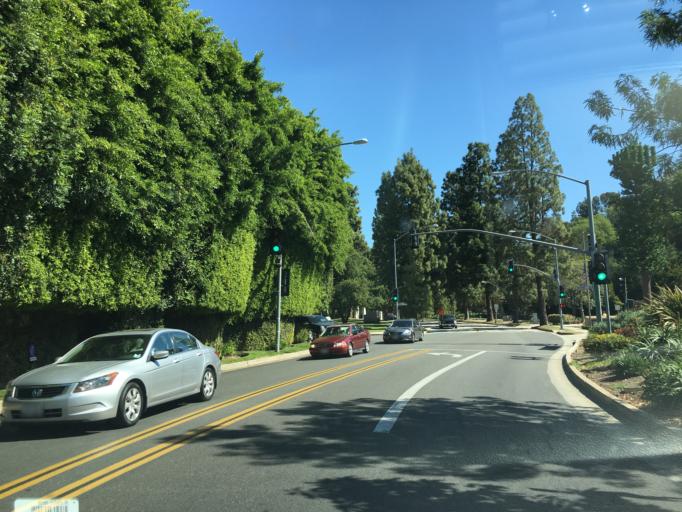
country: US
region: California
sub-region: Los Angeles County
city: Beverly Hills
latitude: 34.0903
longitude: -118.4125
